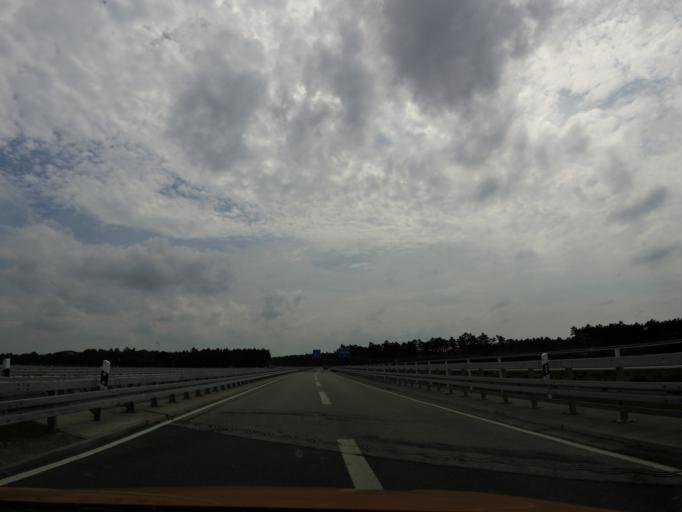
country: DE
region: Mecklenburg-Vorpommern
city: Mirow
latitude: 53.4244
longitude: 11.5205
